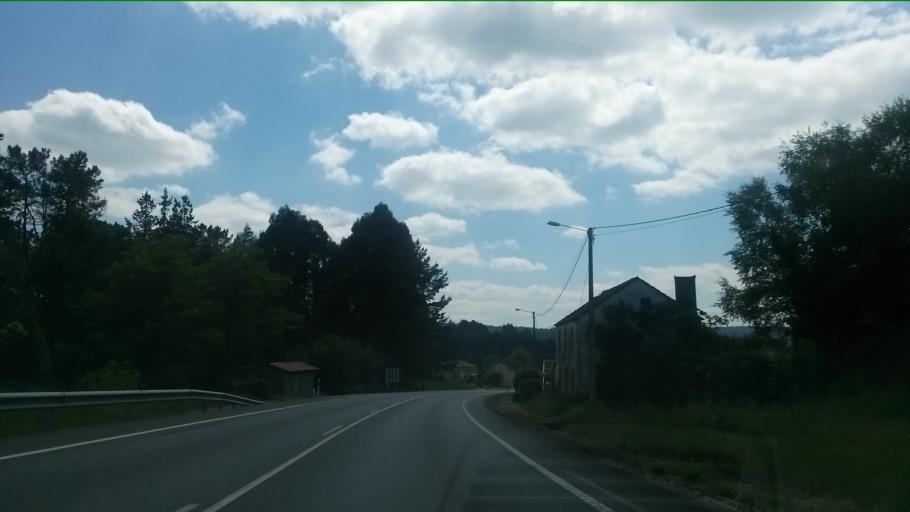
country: ES
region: Galicia
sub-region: Provincia da Coruna
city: Touro
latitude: 42.9509
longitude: -8.3301
